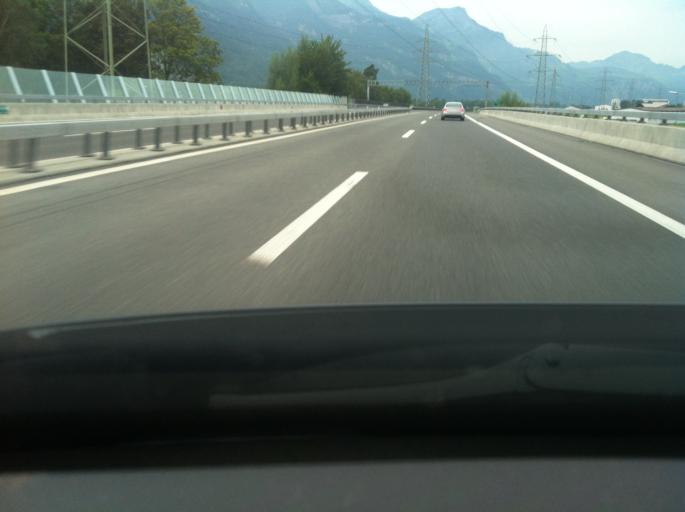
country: CH
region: Uri
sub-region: Uri
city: Attinghausen
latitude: 46.8658
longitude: 8.6321
